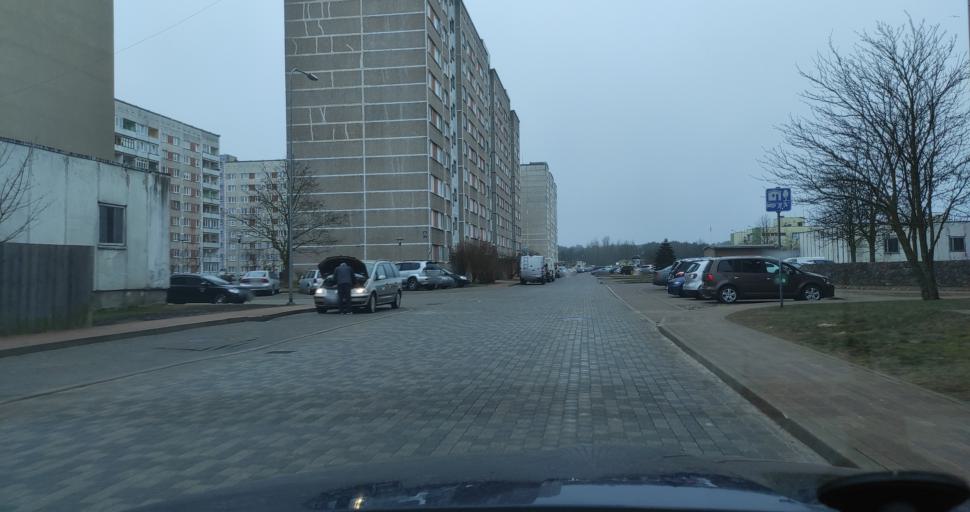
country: LV
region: Ventspils
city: Ventspils
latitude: 57.3840
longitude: 21.5501
